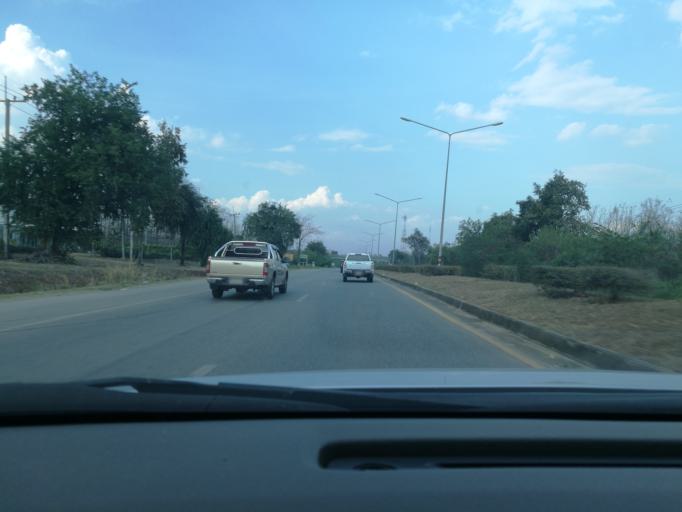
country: TH
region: Phetchabun
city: Phetchabun
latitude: 16.4756
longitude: 101.1590
